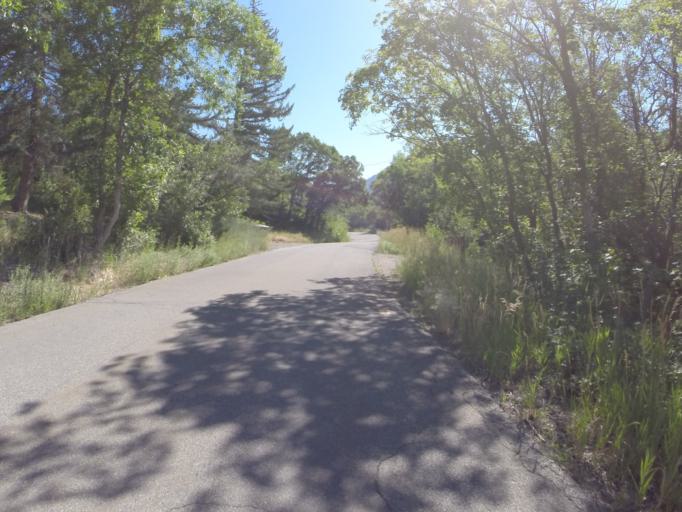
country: US
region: Utah
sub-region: Salt Lake County
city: Salt Lake City
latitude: 40.8062
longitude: -111.8578
